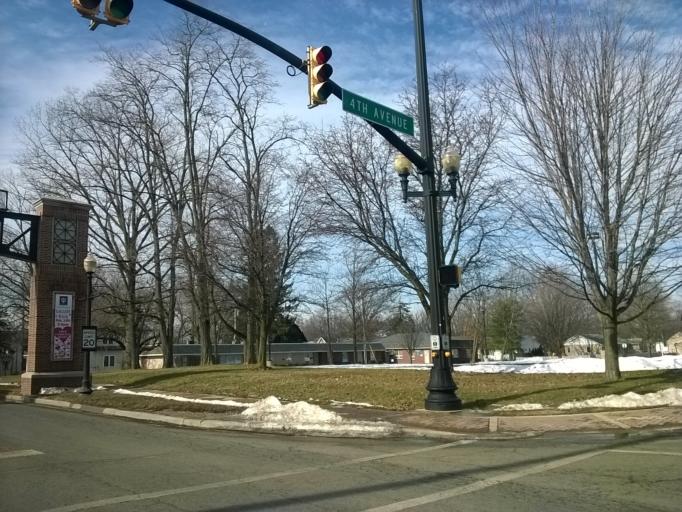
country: US
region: Indiana
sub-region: Hamilton County
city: Carmel
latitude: 39.9784
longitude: -86.1227
